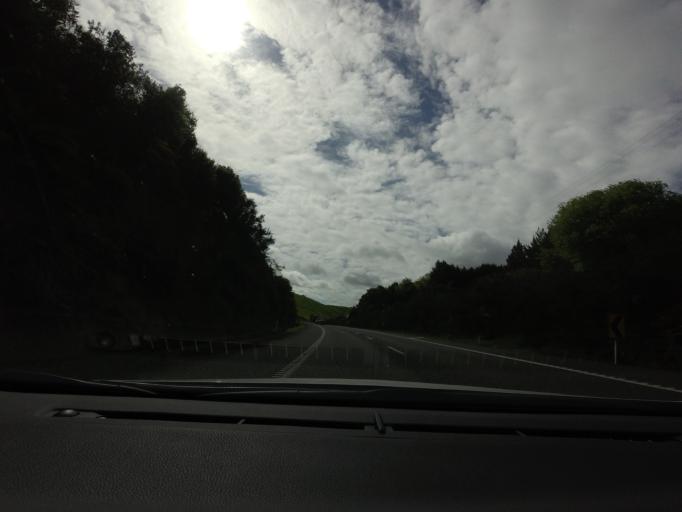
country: NZ
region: Bay of Plenty
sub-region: Rotorua District
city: Rotorua
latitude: -38.2808
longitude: 176.3421
